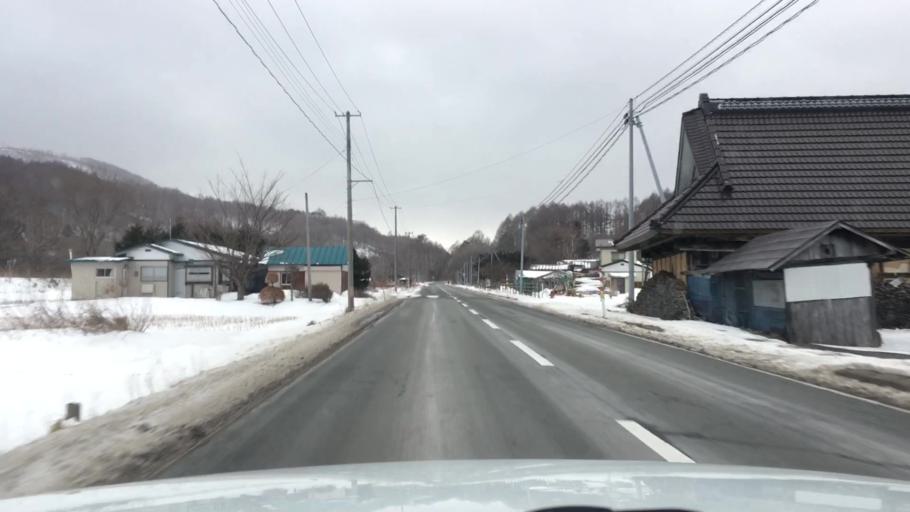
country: JP
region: Iwate
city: Morioka-shi
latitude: 39.6416
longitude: 141.4121
